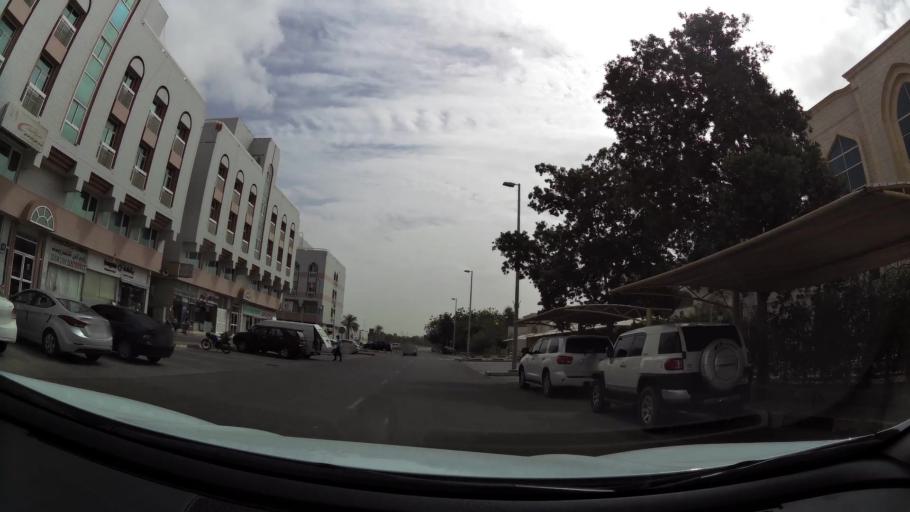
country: AE
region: Abu Dhabi
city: Abu Dhabi
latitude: 24.4055
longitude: 54.5172
